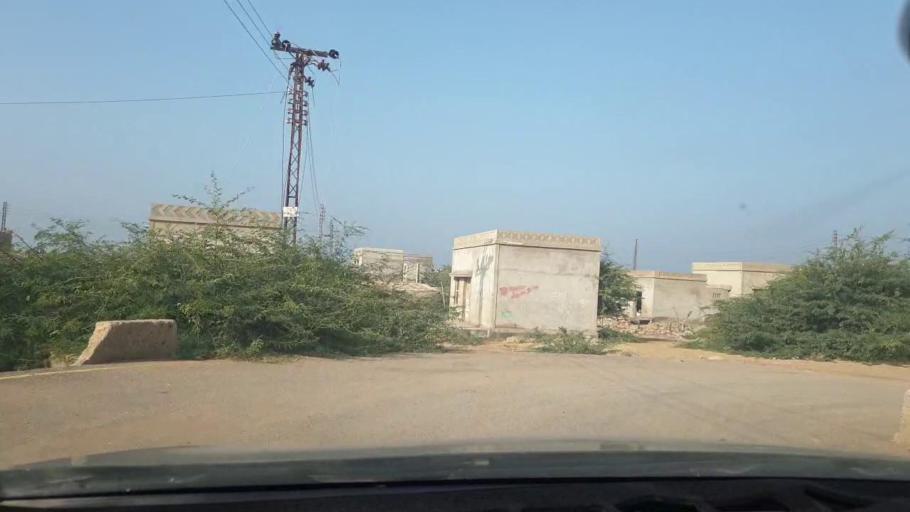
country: PK
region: Balochistan
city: Gadani
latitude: 24.8487
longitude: 66.6612
